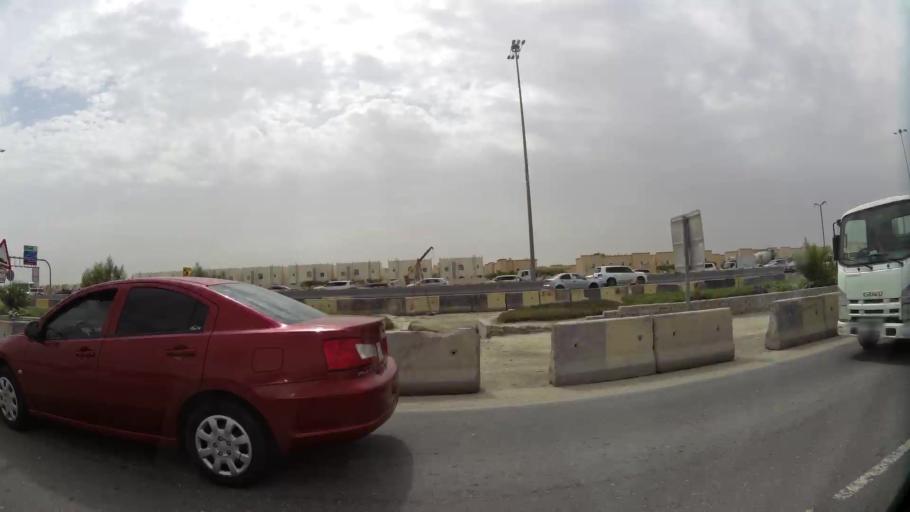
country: QA
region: Baladiyat ar Rayyan
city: Ar Rayyan
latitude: 25.3485
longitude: 51.4565
